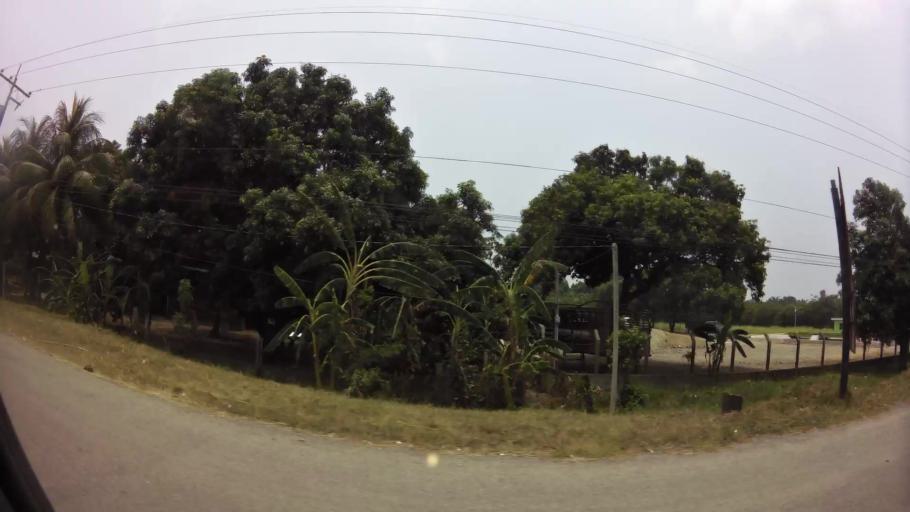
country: HN
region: Yoro
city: El Progreso
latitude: 15.4090
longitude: -87.8368
